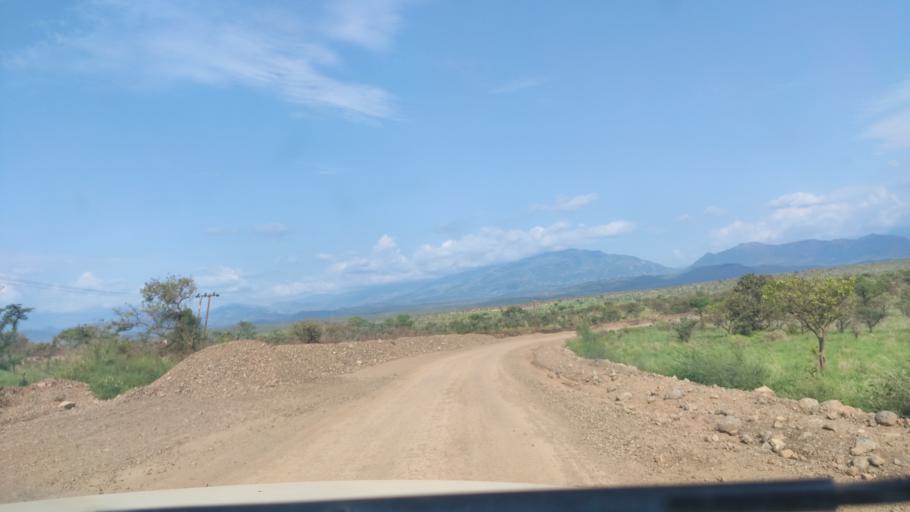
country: ET
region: Southern Nations, Nationalities, and People's Region
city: Felege Neway
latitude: 6.4265
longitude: 37.2262
